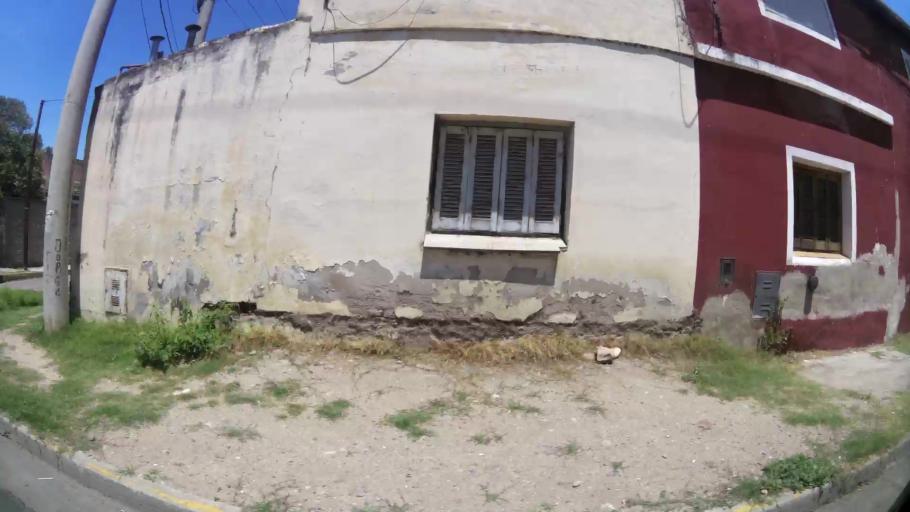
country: AR
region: Cordoba
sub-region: Departamento de Capital
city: Cordoba
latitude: -31.3920
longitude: -64.2072
